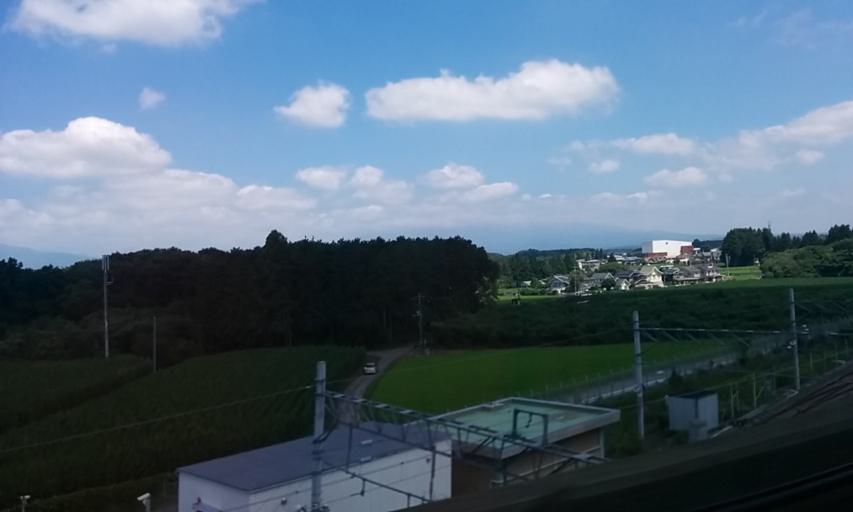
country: JP
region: Tochigi
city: Kuroiso
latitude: 36.9431
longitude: 140.0329
